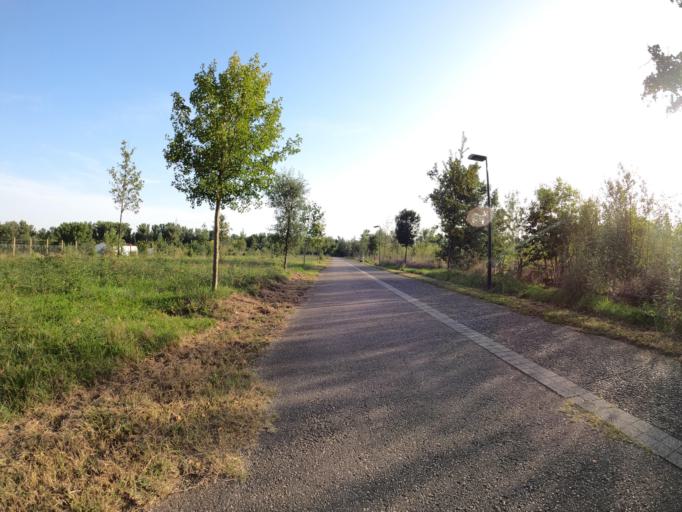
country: FR
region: Midi-Pyrenees
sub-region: Departement de la Haute-Garonne
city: Vieille-Toulouse
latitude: 43.5518
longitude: 1.4302
